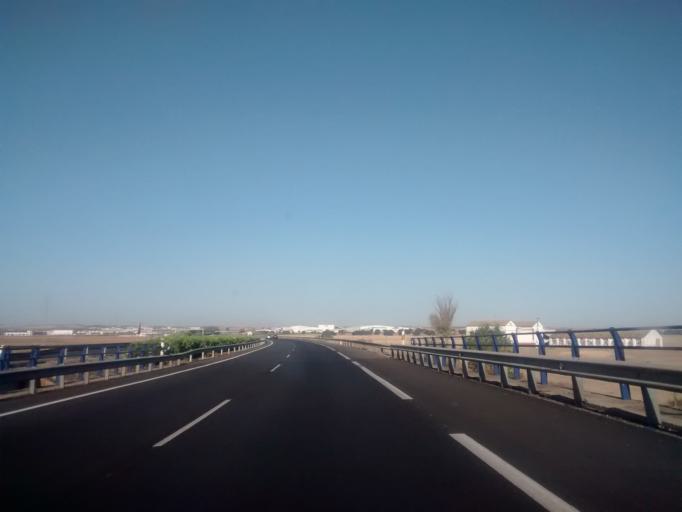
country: ES
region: Andalusia
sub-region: Provincia de Sevilla
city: Sanlucar la Mayor
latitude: 37.3715
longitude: -6.2310
